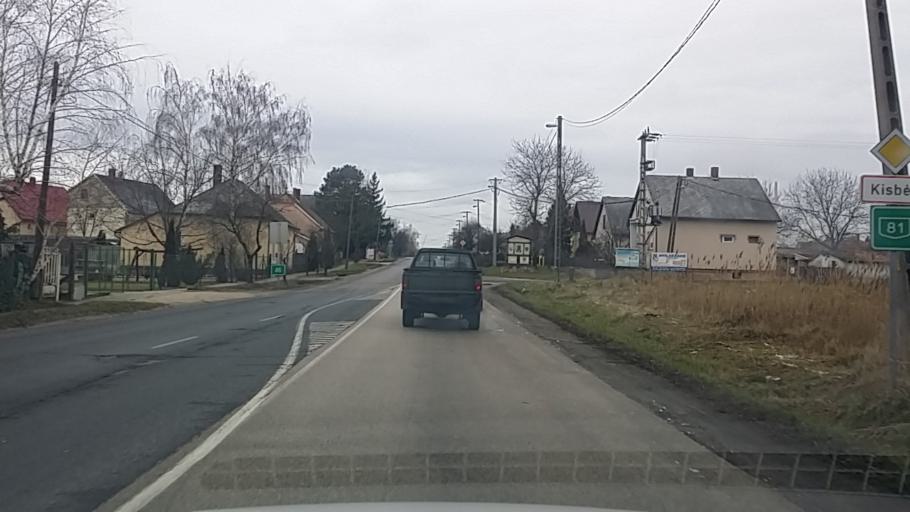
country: HU
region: Komarom-Esztergom
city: Kisber
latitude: 47.5064
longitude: 18.0431
